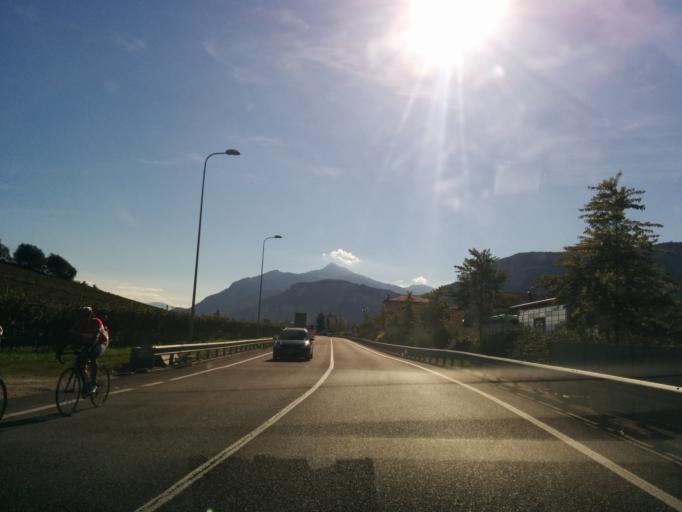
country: IT
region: Trentino-Alto Adige
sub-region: Provincia di Trento
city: Zambana
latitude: 46.1501
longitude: 11.1004
